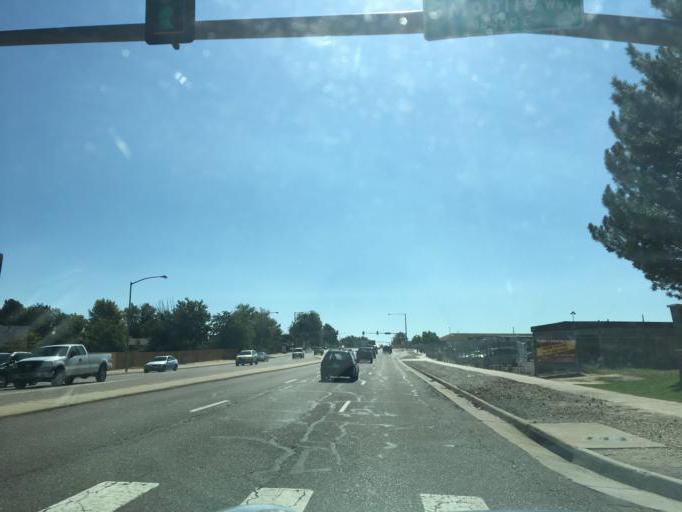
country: US
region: Colorado
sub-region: Arapahoe County
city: Dove Valley
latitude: 39.6285
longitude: -104.7987
